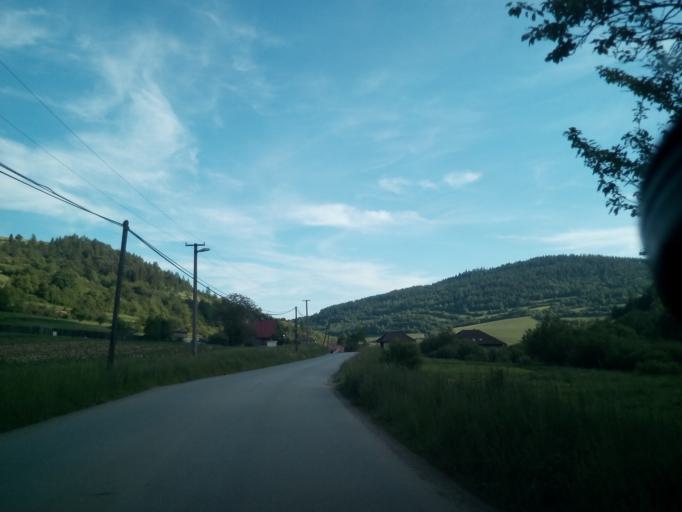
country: SK
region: Presovsky
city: Lipany
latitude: 49.0456
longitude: 20.9453
